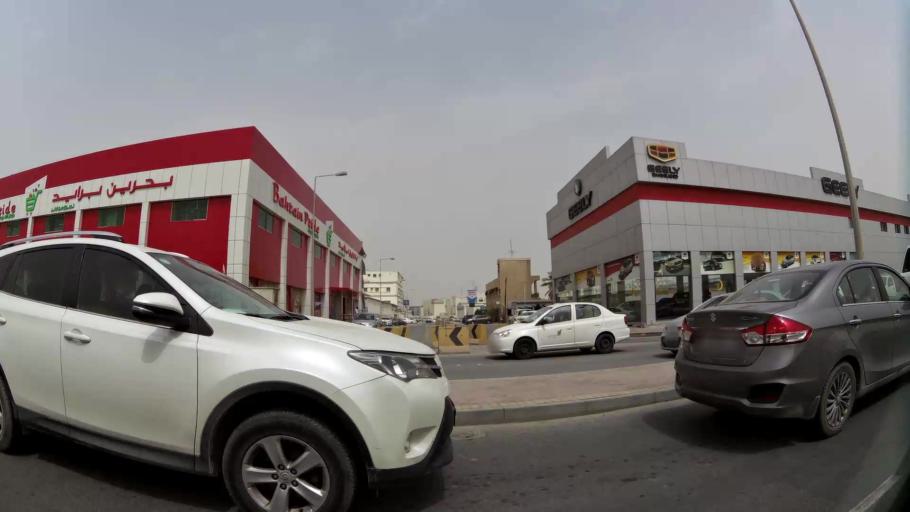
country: BH
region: Northern
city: Madinat `Isa
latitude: 26.1868
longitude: 50.5381
